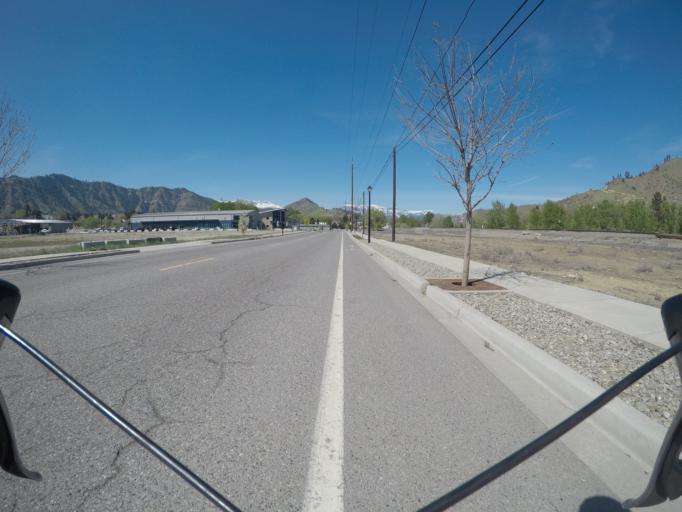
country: US
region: Washington
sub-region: Chelan County
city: Cashmere
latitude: 47.5216
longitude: -120.4781
